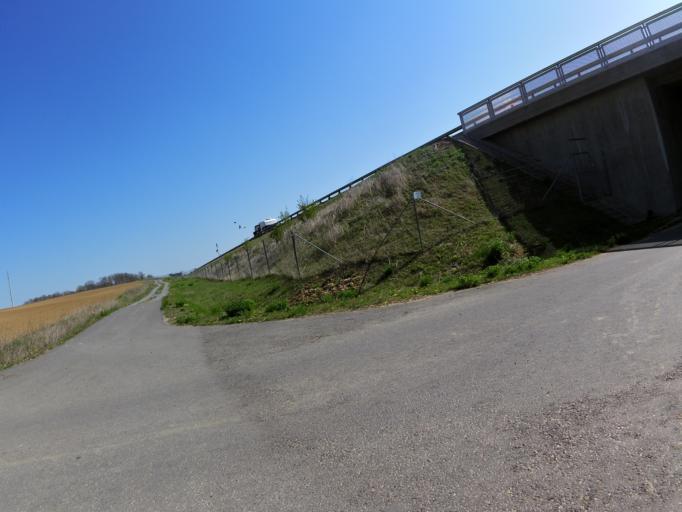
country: DE
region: Bavaria
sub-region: Regierungsbezirk Unterfranken
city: Biebelried
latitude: 49.7718
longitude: 10.0728
